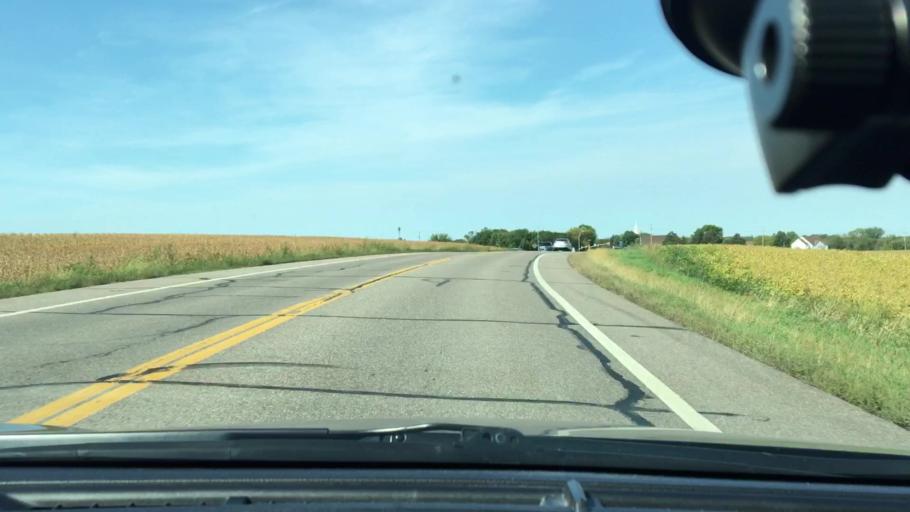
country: US
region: Minnesota
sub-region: Hennepin County
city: Corcoran
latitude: 45.0919
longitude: -93.5394
